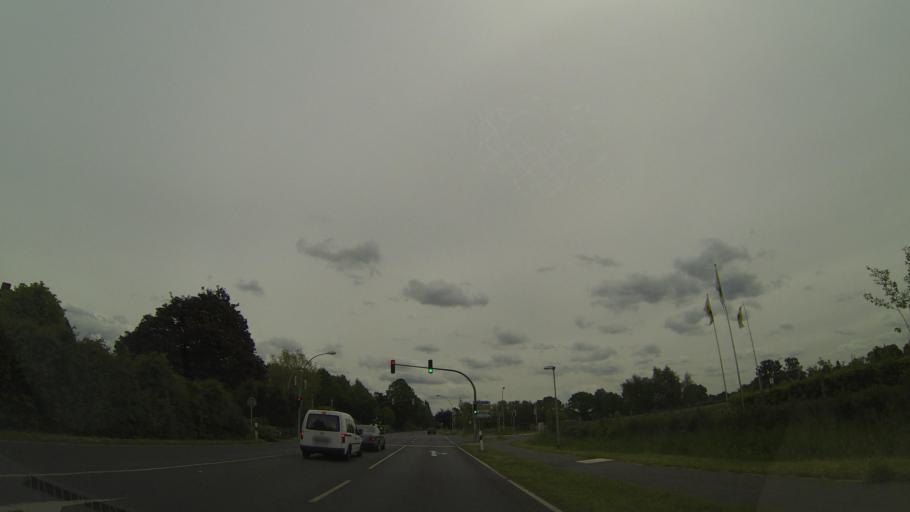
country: DE
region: Schleswig-Holstein
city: Ellerbek
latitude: 53.6480
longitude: 9.8716
